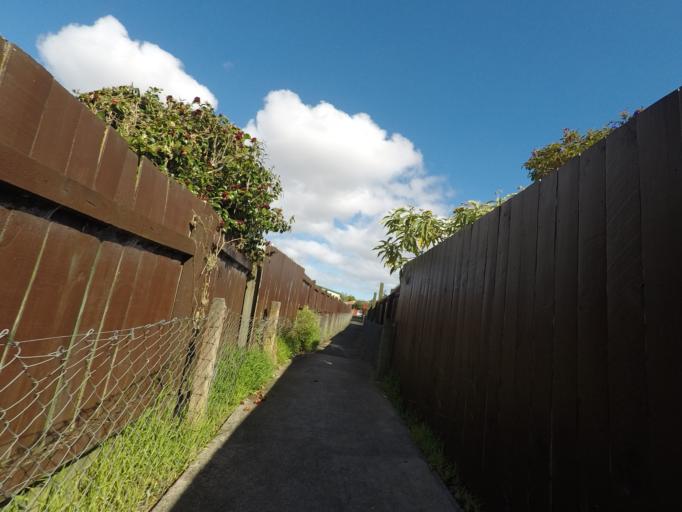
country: NZ
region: Auckland
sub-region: Auckland
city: Rosebank
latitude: -36.8599
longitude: 174.6018
